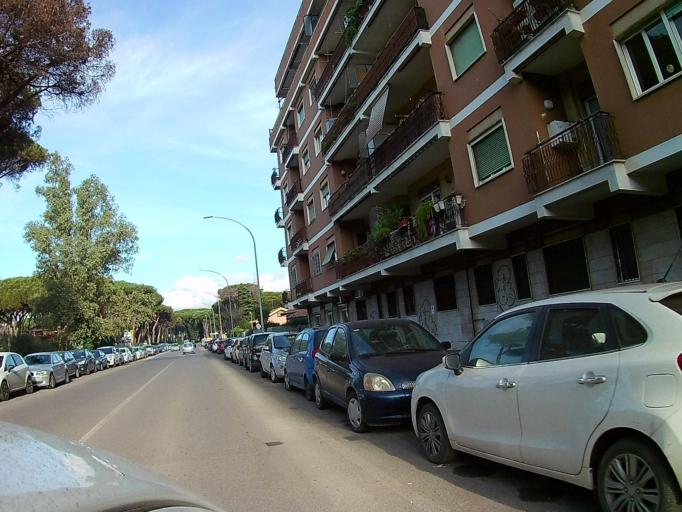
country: IT
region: Latium
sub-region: Citta metropolitana di Roma Capitale
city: Lido di Ostia
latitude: 41.7399
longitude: 12.2804
